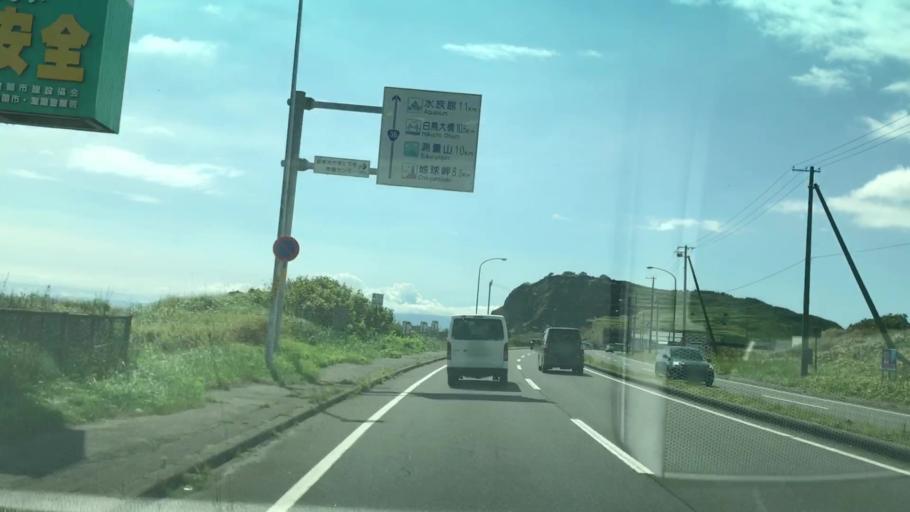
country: JP
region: Hokkaido
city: Muroran
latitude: 42.3463
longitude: 141.0378
